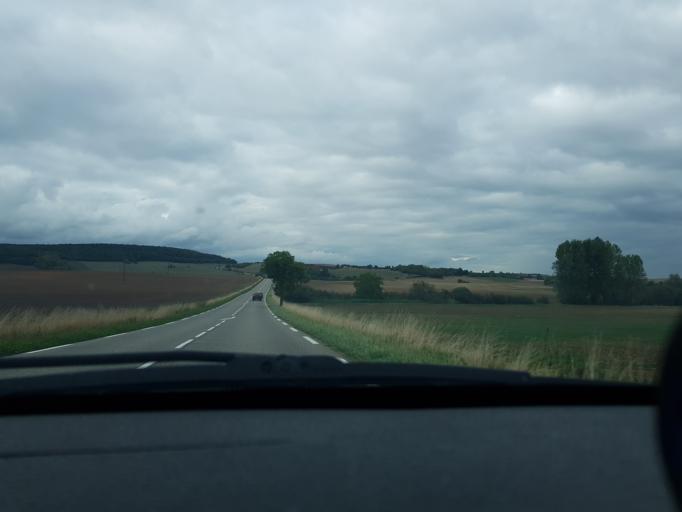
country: FR
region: Lorraine
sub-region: Departement de la Moselle
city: Chateau-Salins
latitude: 48.8693
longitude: 6.5319
